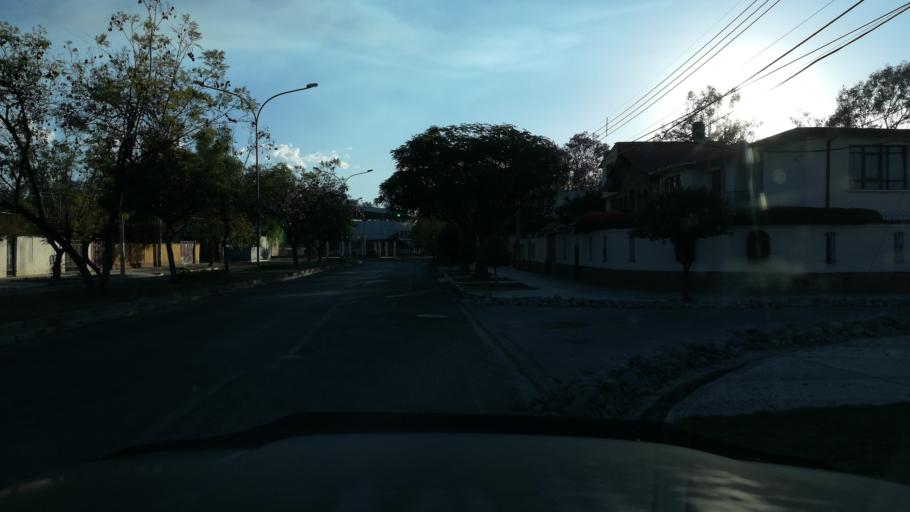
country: BO
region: Cochabamba
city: Cochabamba
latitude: -17.3991
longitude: -66.1715
